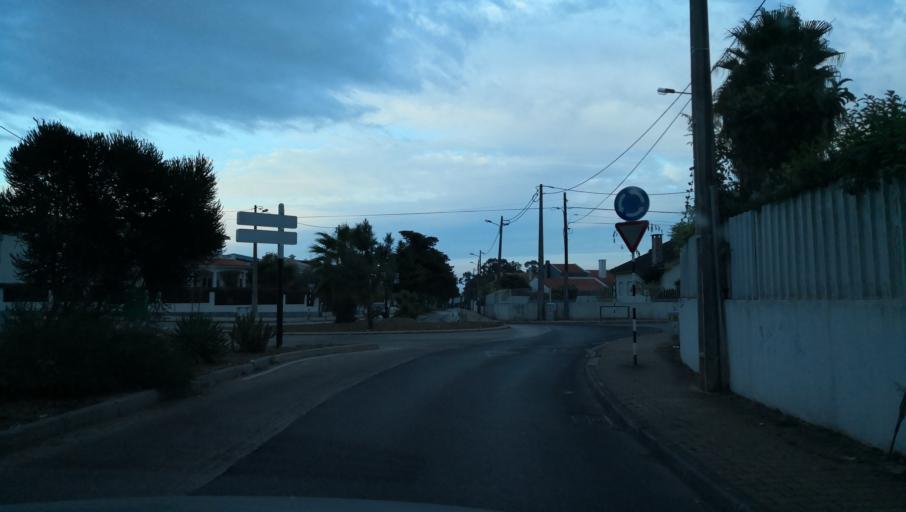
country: PT
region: Setubal
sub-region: Almada
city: Charneca
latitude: 38.6006
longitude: -9.1761
